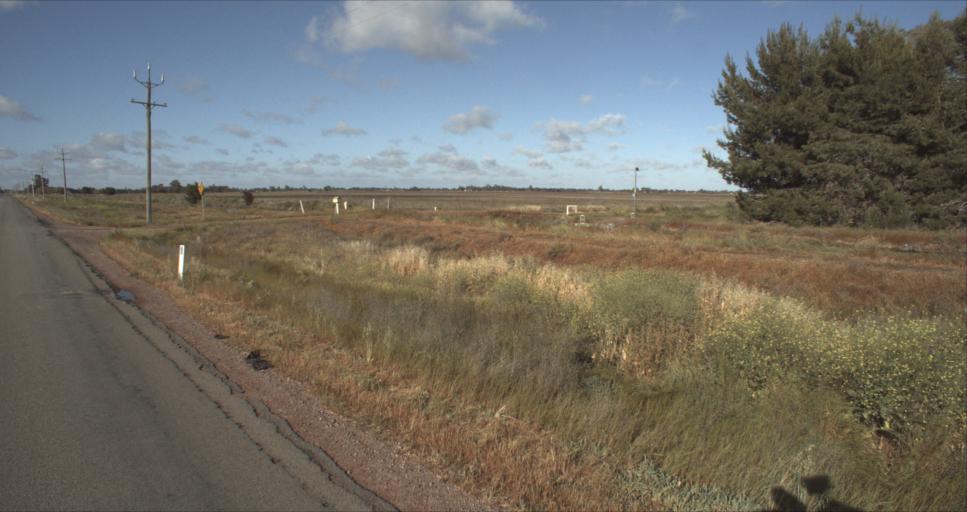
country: AU
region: New South Wales
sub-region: Leeton
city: Leeton
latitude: -34.5236
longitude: 146.3901
